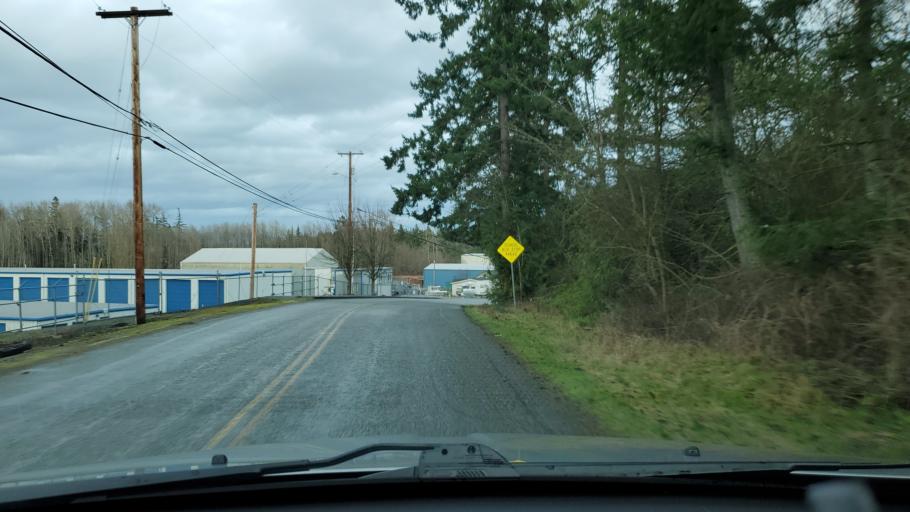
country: US
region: Washington
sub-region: Skagit County
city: Anacortes
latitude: 48.4584
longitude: -122.5539
